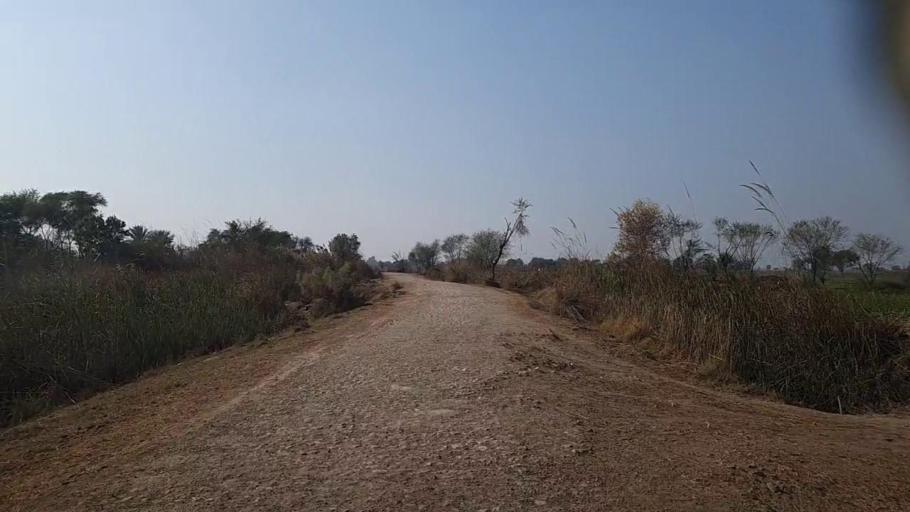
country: PK
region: Sindh
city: Mirpur Mathelo
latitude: 27.9038
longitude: 69.6148
